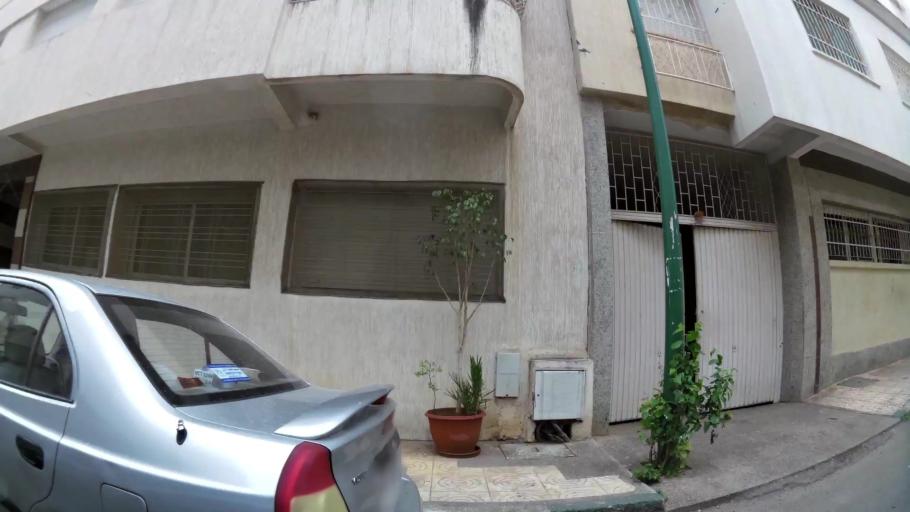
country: MA
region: Fes-Boulemane
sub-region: Fes
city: Fes
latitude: 34.0277
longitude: -4.9958
